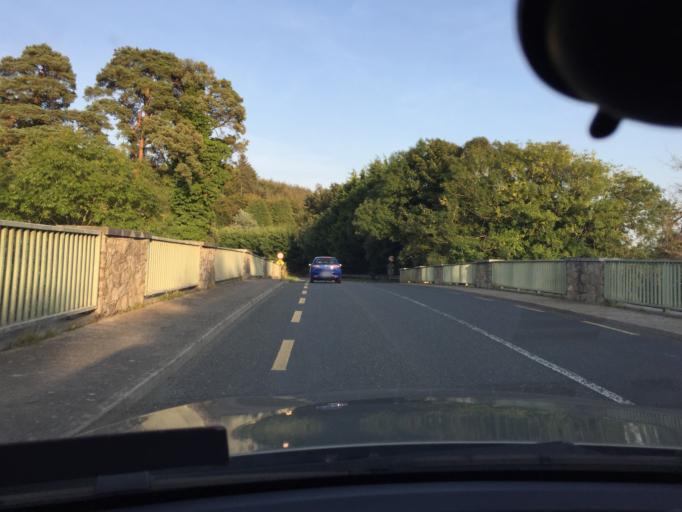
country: IE
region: Leinster
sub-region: Wicklow
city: Rathdrum
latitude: 53.0313
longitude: -6.2532
